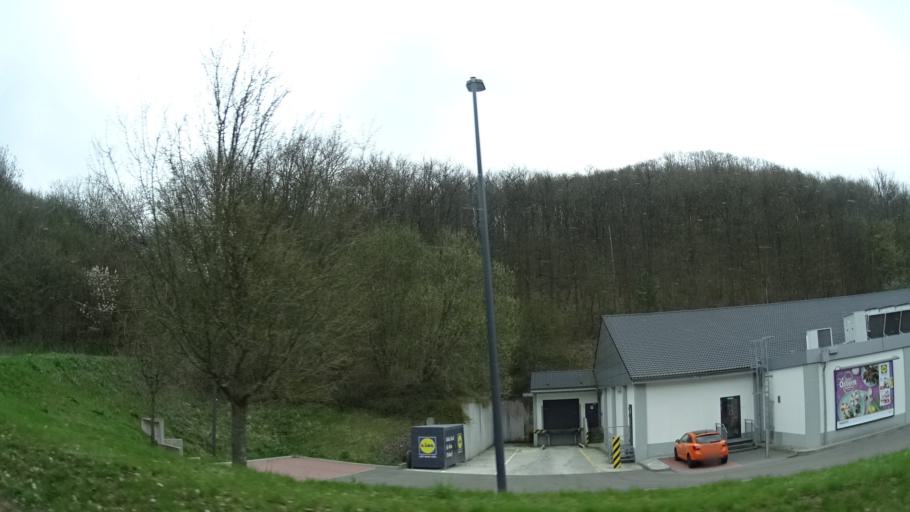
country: DE
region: Rheinland-Pfalz
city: Vollmersbach
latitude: 49.7291
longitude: 7.3207
